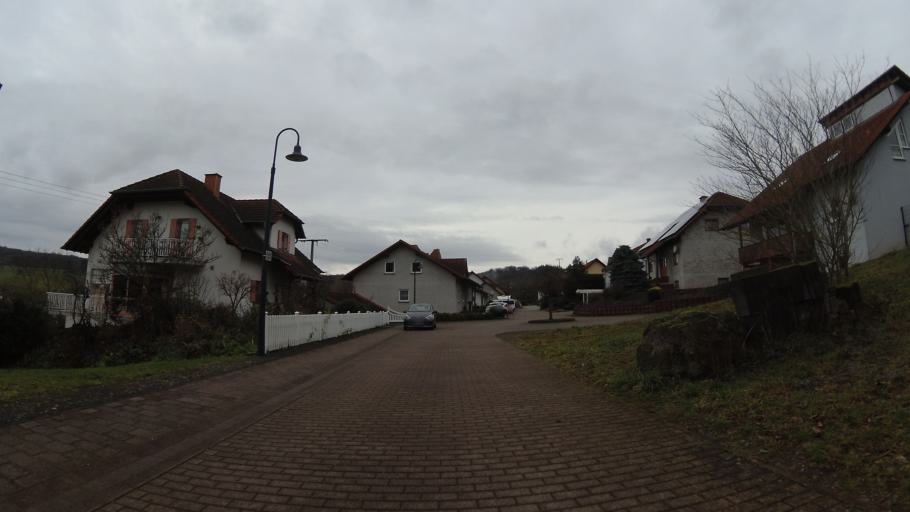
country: DE
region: Rheinland-Pfalz
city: Frohnhofen
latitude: 49.4552
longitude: 7.3011
